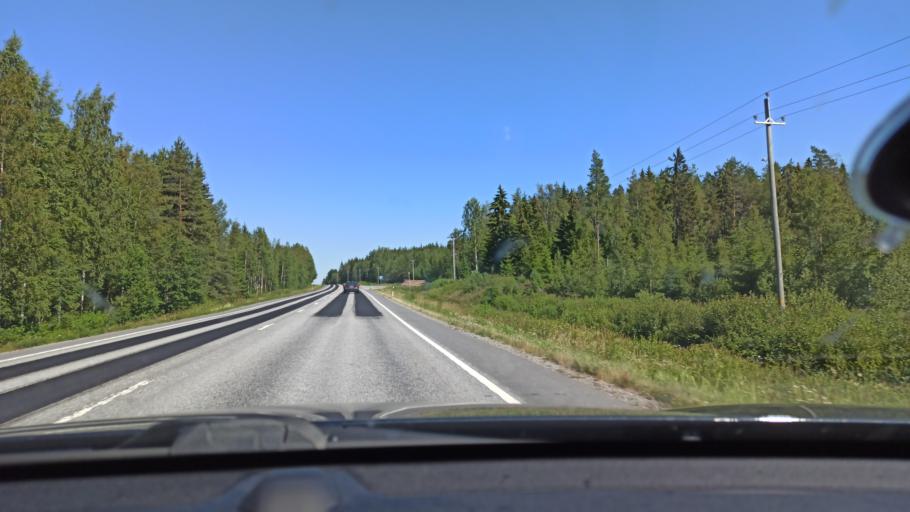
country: FI
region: Ostrobothnia
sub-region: Vaasa
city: Voera
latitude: 63.2048
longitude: 22.1365
